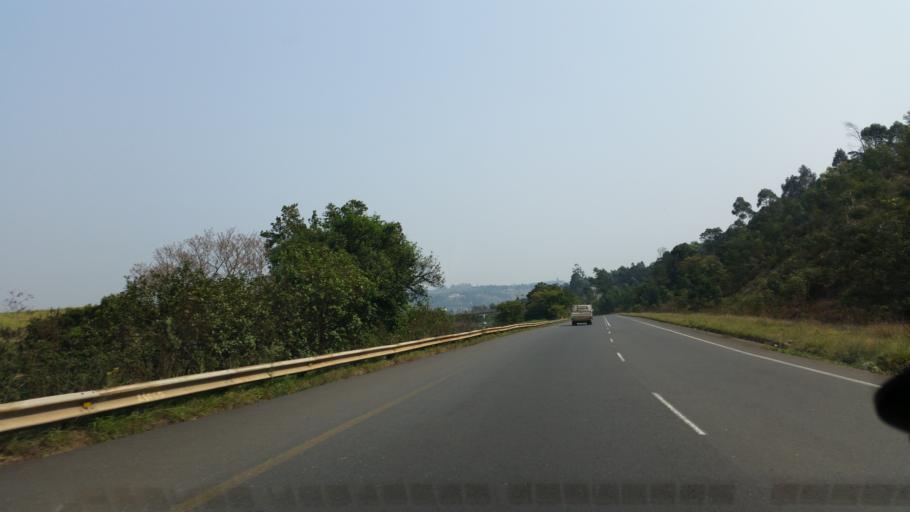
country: ZA
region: KwaZulu-Natal
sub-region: eThekwini Metropolitan Municipality
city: Mpumalanga
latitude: -29.8017
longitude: 30.7672
